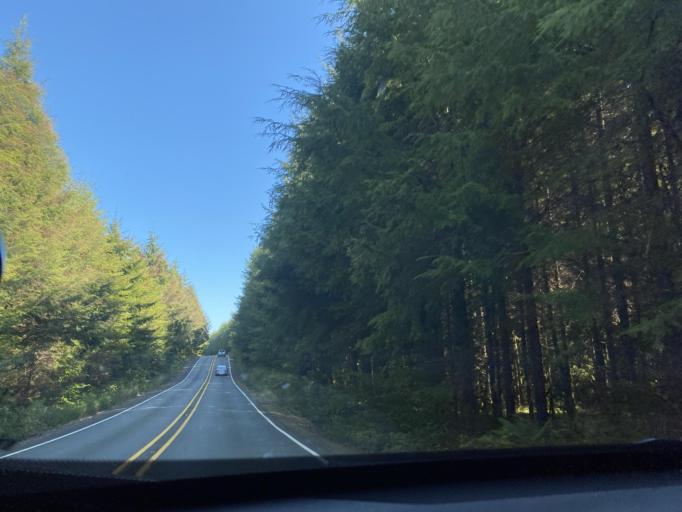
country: US
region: Washington
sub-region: Clallam County
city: Forks
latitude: 47.9197
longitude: -124.5146
